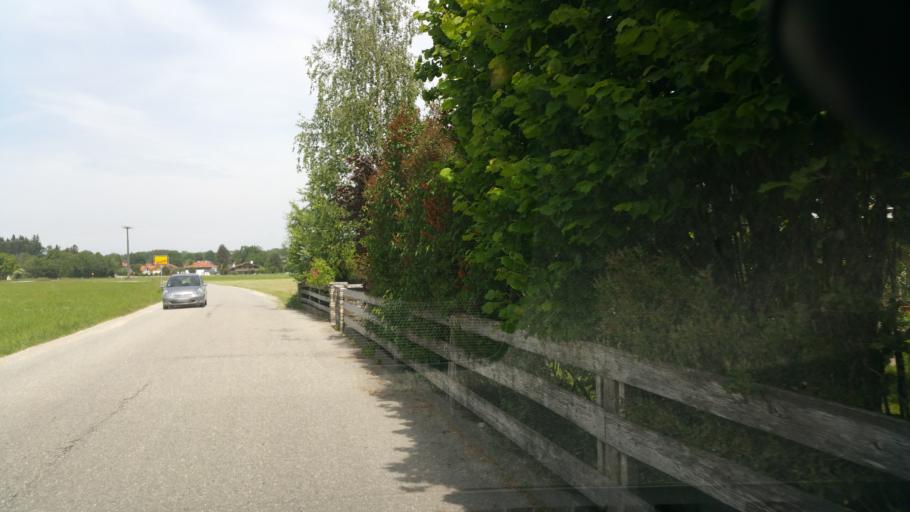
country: DE
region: Bavaria
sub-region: Upper Bavaria
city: Aschau im Chiemgau
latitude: 47.7864
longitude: 12.3283
